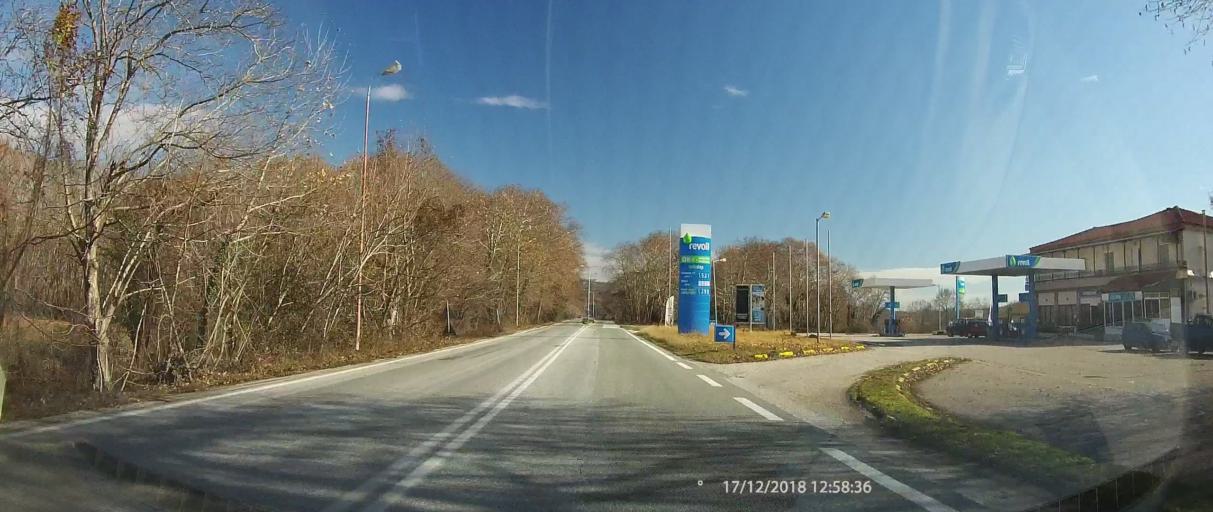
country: GR
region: Thessaly
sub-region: Trikala
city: Kastraki
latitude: 39.7389
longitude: 21.5447
